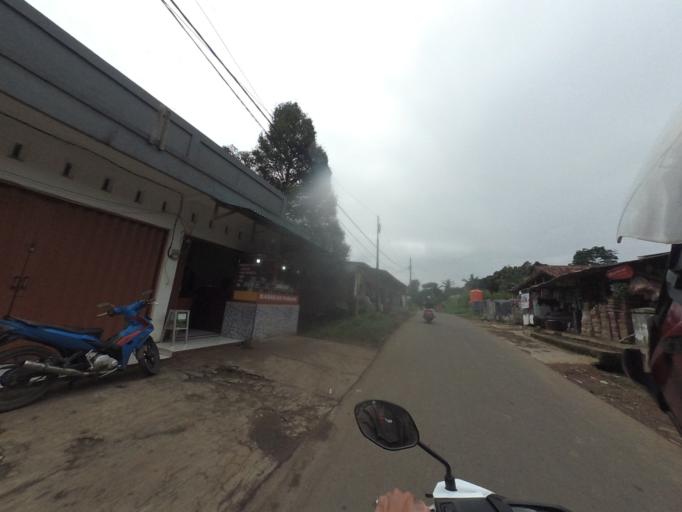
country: ID
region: West Java
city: Bogor
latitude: -6.6383
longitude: 106.7413
